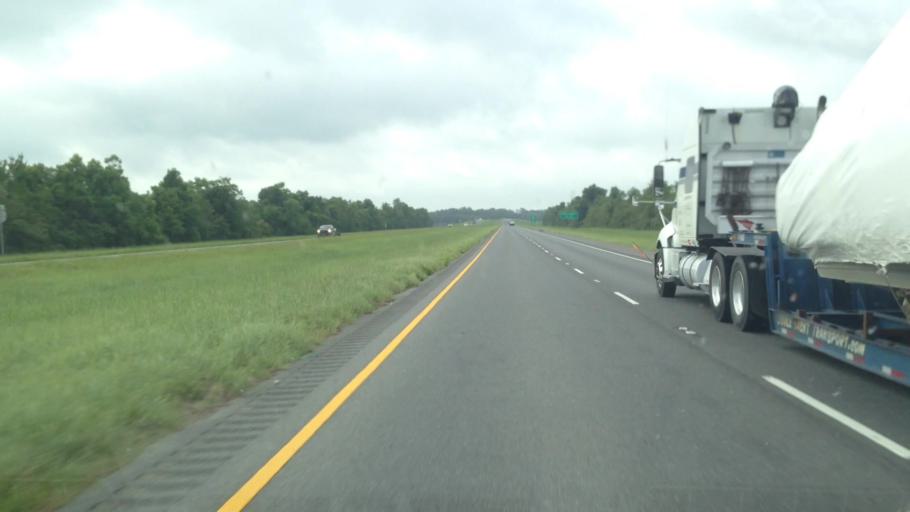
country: US
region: Louisiana
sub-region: Saint Landry Parish
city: Opelousas
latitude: 30.6508
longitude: -92.0575
